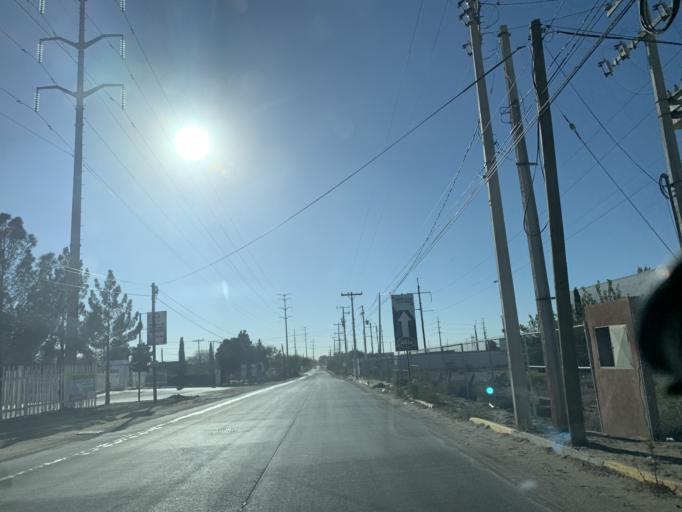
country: US
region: Texas
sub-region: El Paso County
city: Socorro
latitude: 31.7081
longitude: -106.3751
